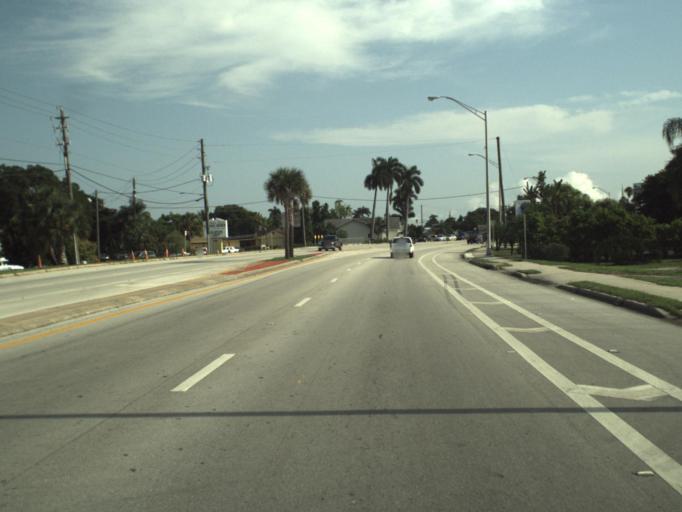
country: US
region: Florida
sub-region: Palm Beach County
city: Belle Glade
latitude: 26.6769
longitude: -80.6703
